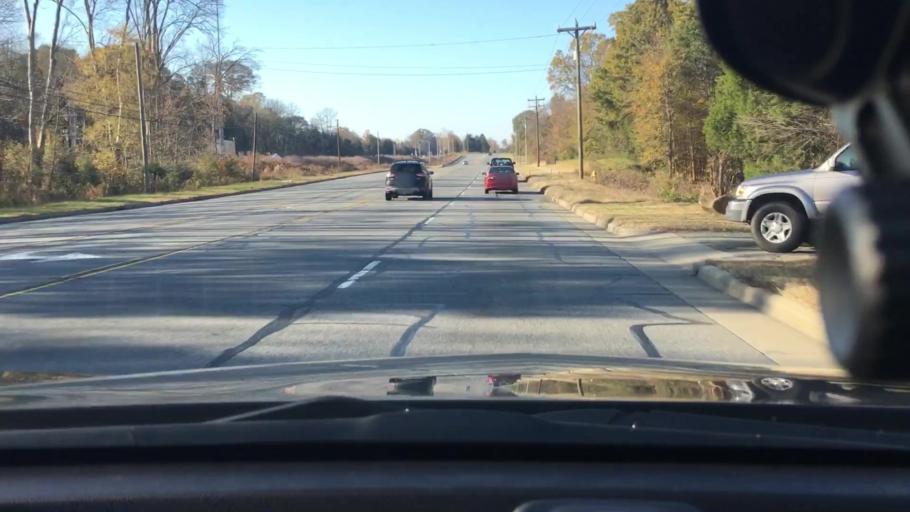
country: US
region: North Carolina
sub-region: Cabarrus County
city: Harrisburg
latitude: 35.3292
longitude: -80.6330
